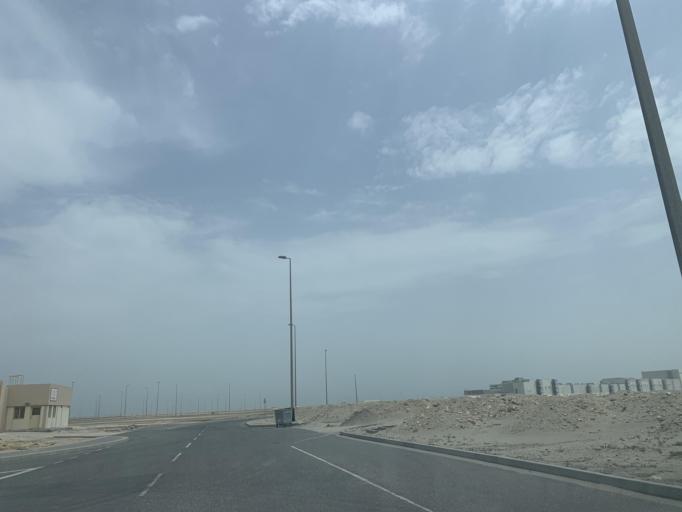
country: BH
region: Muharraq
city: Al Hadd
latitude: 26.2202
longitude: 50.6922
